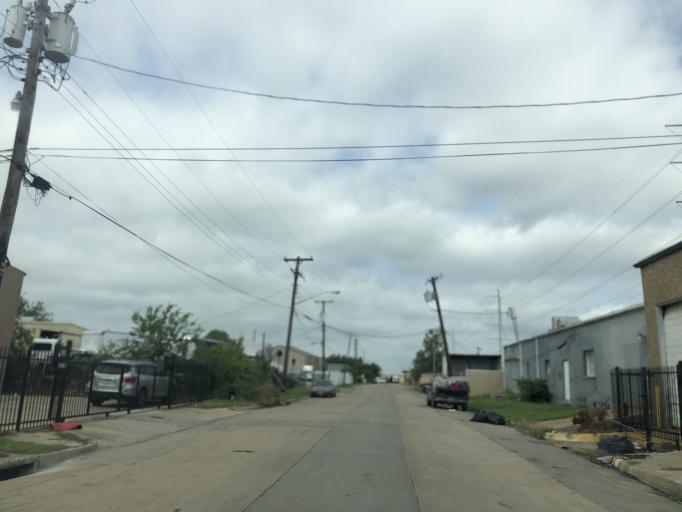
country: US
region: Texas
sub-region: Dallas County
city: Cockrell Hill
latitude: 32.8075
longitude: -96.8756
